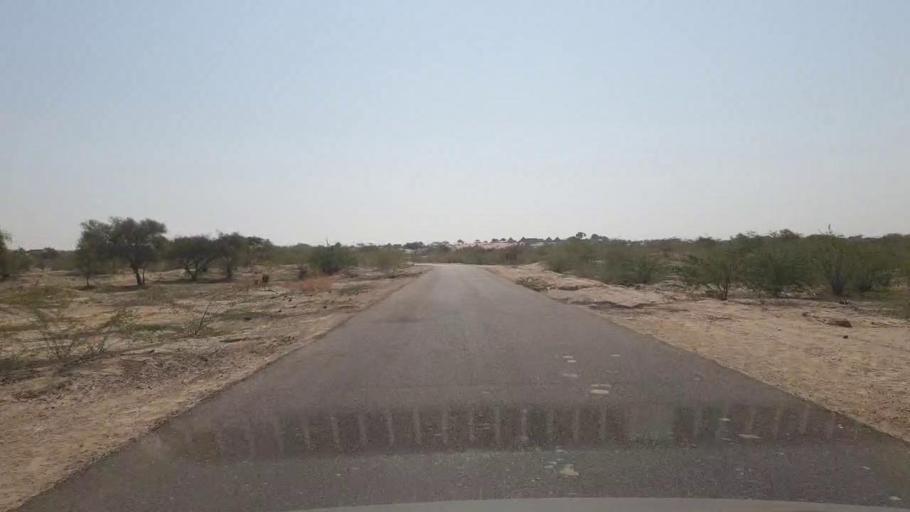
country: PK
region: Sindh
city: Chor
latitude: 25.5871
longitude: 70.1847
